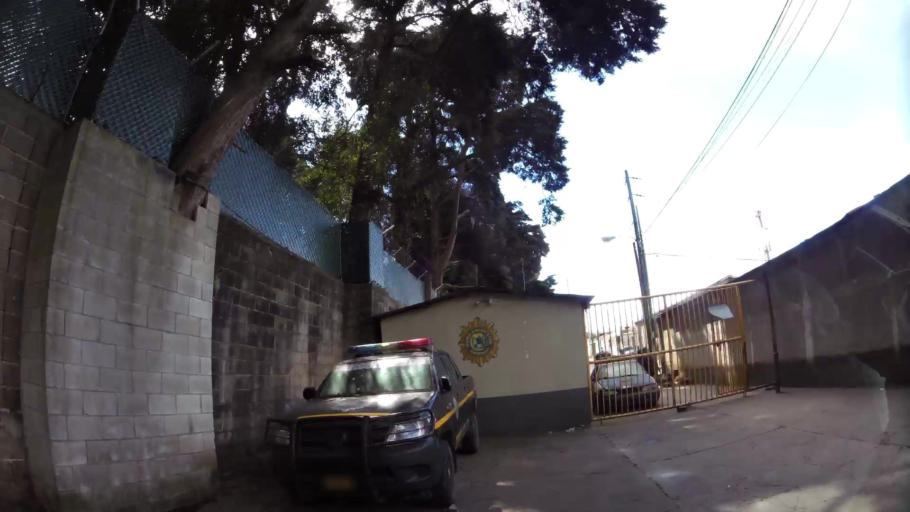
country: GT
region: Guatemala
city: Mixco
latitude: 14.6363
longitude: -90.5700
